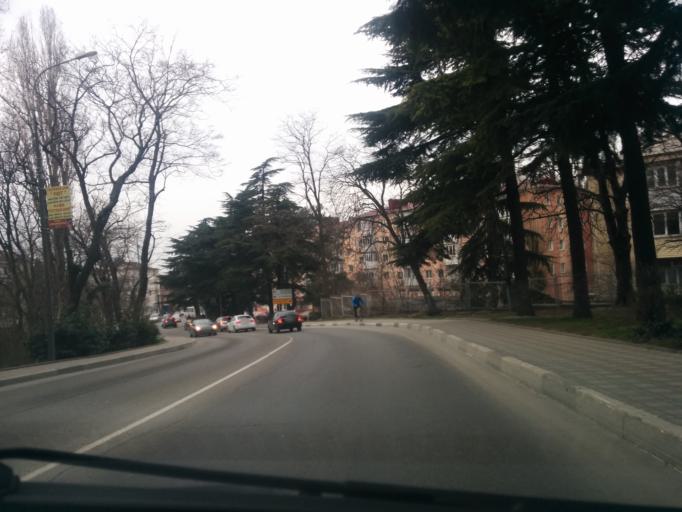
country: RU
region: Krasnodarskiy
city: Tuapse
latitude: 44.1016
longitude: 39.0843
